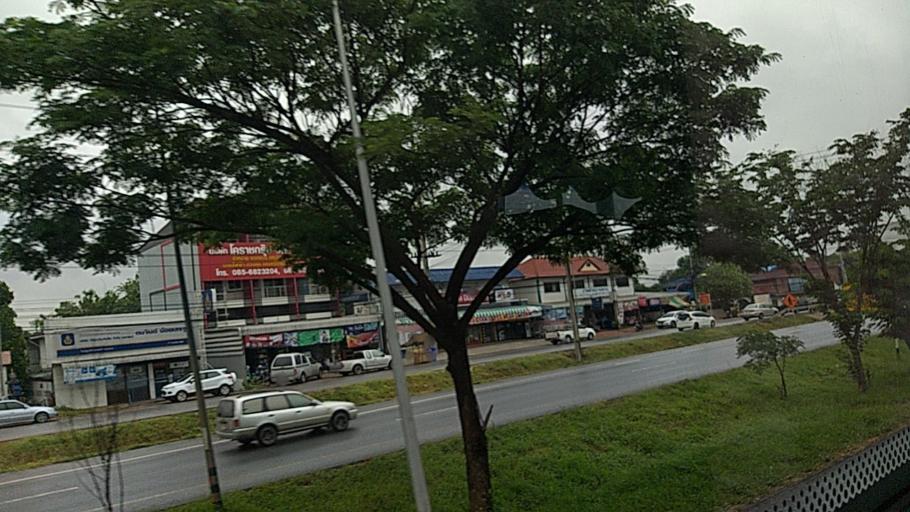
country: TH
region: Nakhon Ratchasima
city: Nakhon Ratchasima
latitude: 14.9750
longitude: 102.0520
